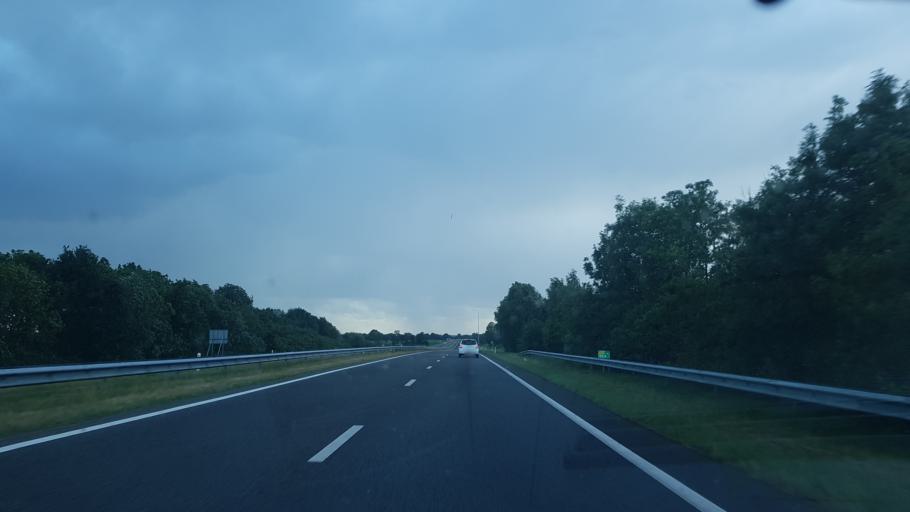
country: NL
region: Friesland
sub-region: Gemeente Smallingerland
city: Oudega
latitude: 53.1456
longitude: 6.0224
